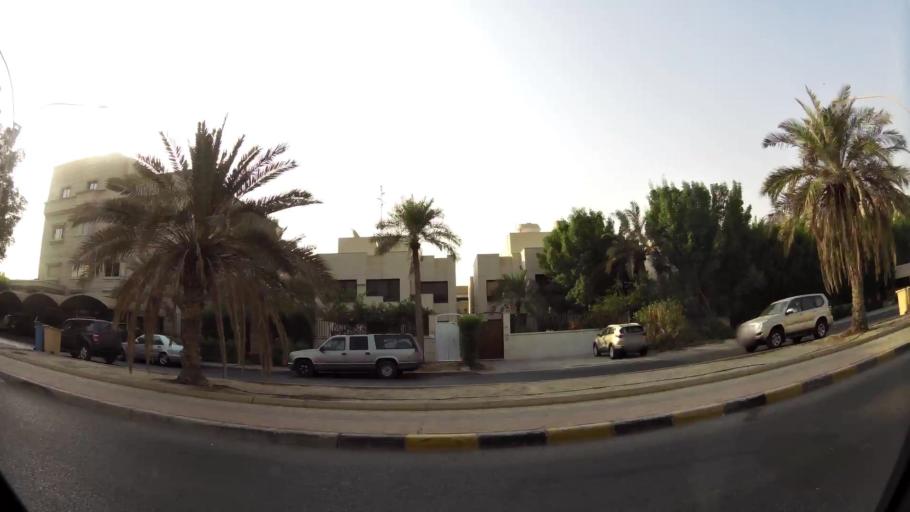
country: KW
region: Muhafazat Hawalli
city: Salwa
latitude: 29.3038
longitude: 48.0778
